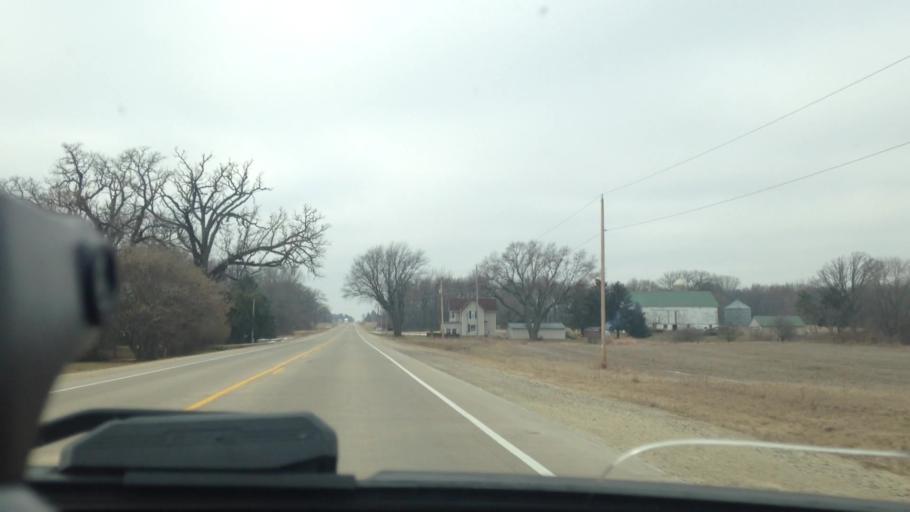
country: US
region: Wisconsin
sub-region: Dodge County
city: Horicon
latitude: 43.4735
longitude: -88.6890
